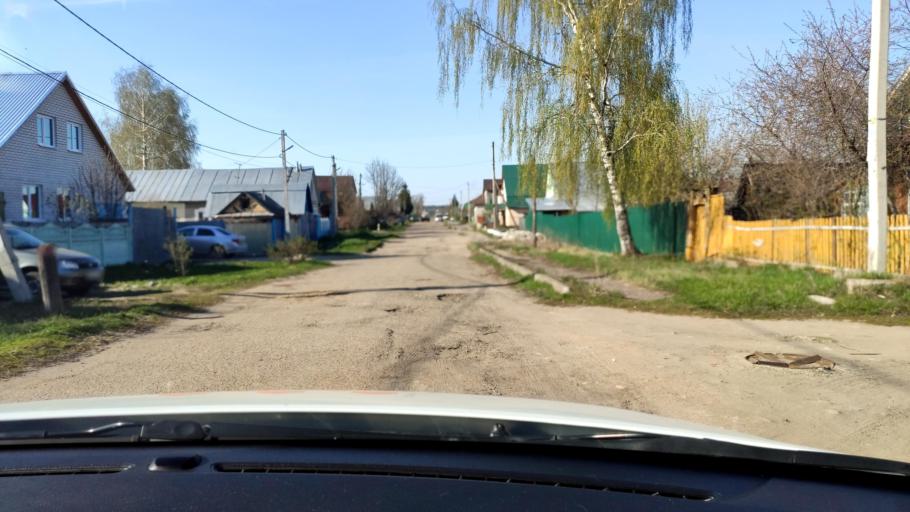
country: RU
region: Tatarstan
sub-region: Gorod Kazan'
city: Kazan
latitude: 55.8731
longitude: 49.0607
